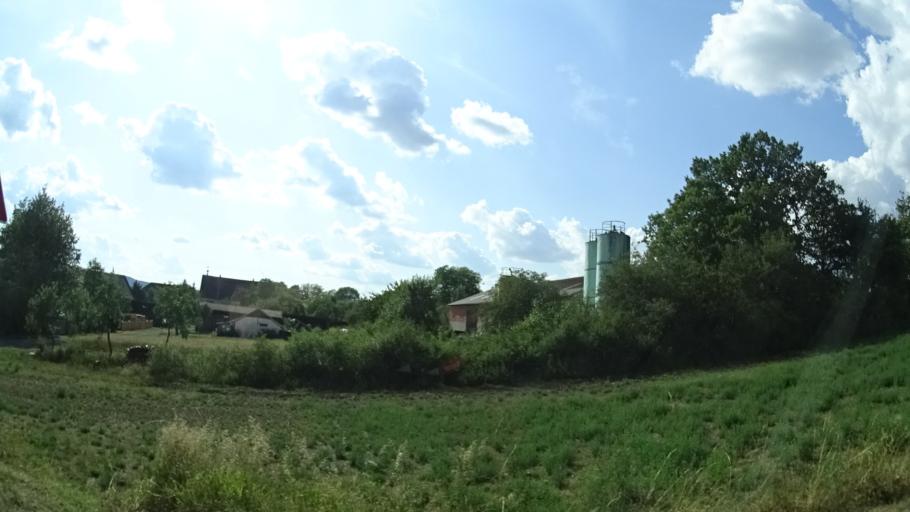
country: DE
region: Bavaria
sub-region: Regierungsbezirk Unterfranken
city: Bundorf
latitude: 50.2687
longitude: 10.5410
